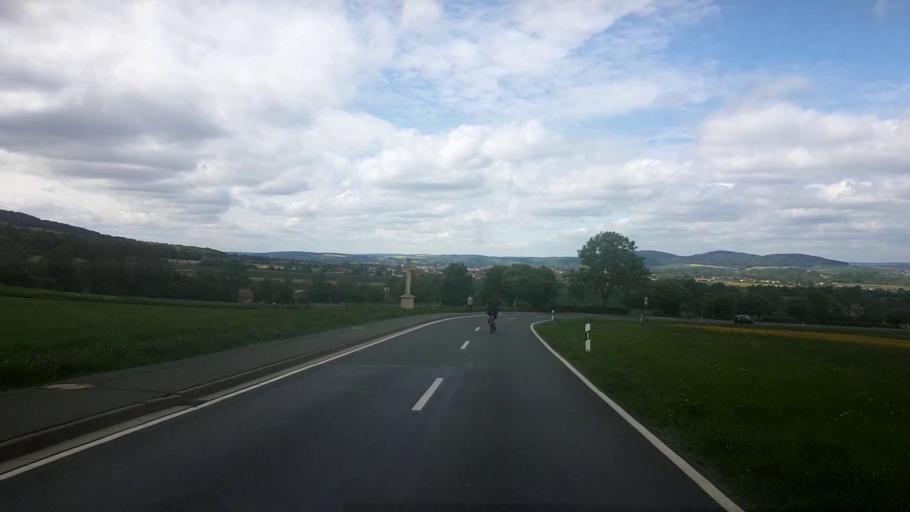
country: DE
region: Bavaria
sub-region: Upper Franconia
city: Lichtenfels
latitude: 50.1193
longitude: 11.0462
